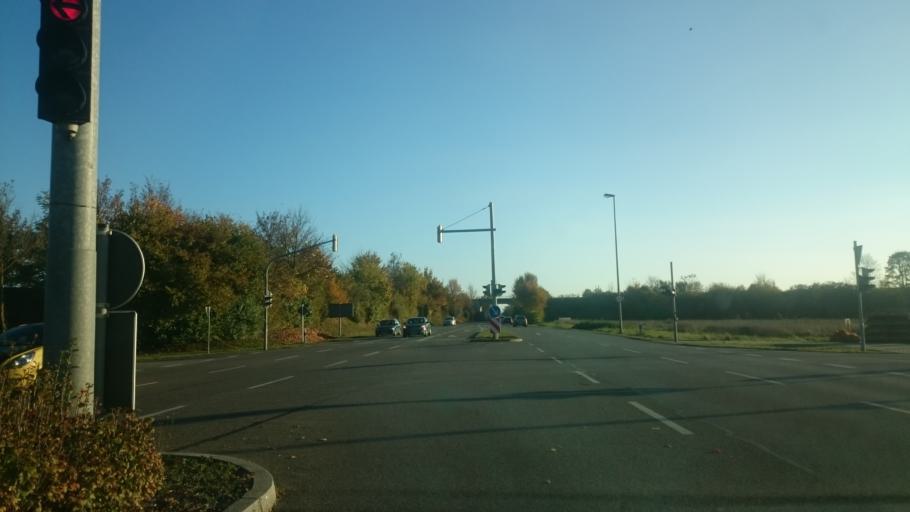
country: DE
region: Bavaria
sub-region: Swabia
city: Friedberg
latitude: 48.3539
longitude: 10.9658
